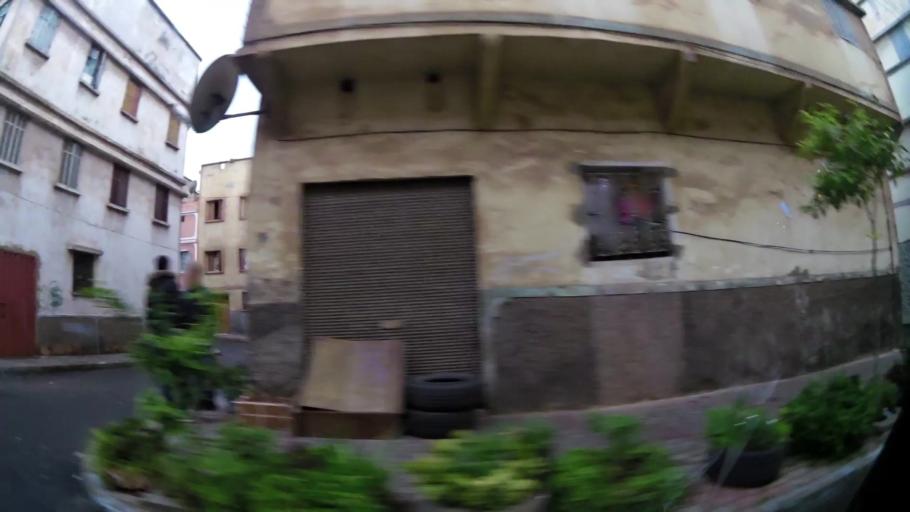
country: MA
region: Grand Casablanca
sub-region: Casablanca
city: Casablanca
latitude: 33.5535
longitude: -7.5856
